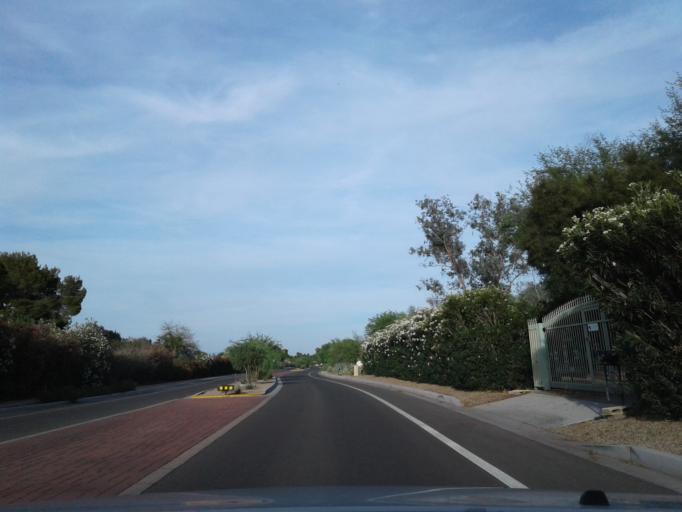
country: US
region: Arizona
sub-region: Maricopa County
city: Paradise Valley
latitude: 33.5608
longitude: -111.9674
